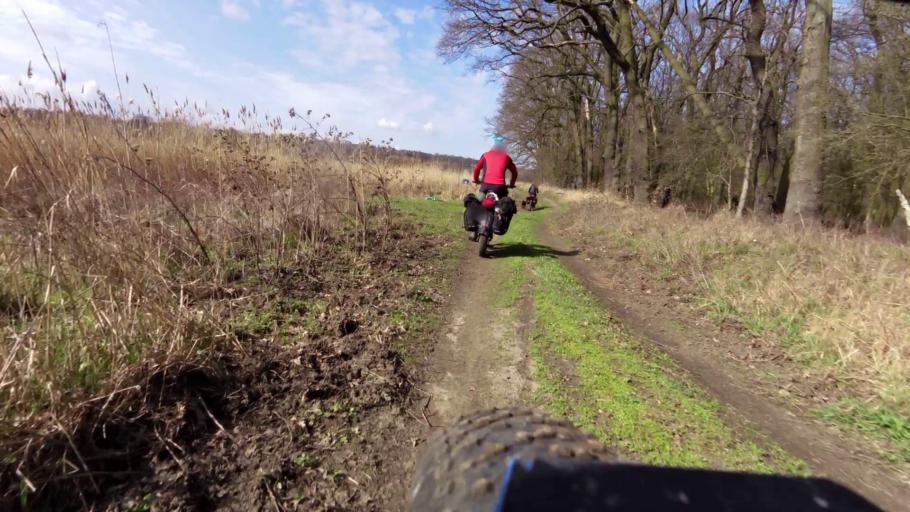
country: PL
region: Lubusz
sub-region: Powiat slubicki
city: Slubice
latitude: 52.3269
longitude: 14.5682
